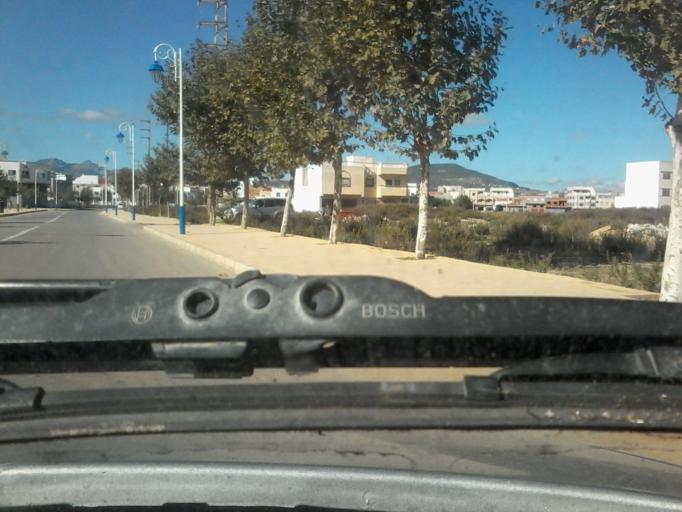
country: MA
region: Tanger-Tetouan
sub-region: Tetouan
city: Martil
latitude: 35.6948
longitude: -5.3430
